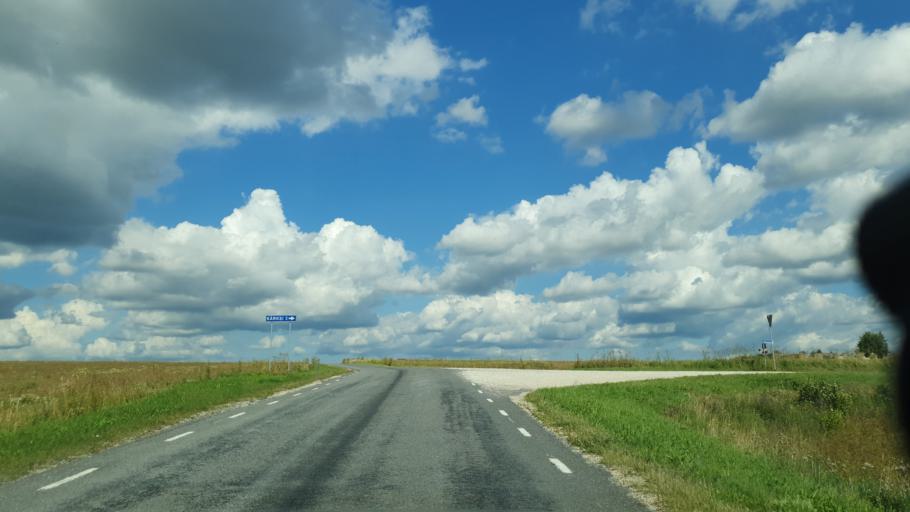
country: EE
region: Jogevamaa
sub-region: Tabivere vald
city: Tabivere
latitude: 58.6240
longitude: 26.5792
